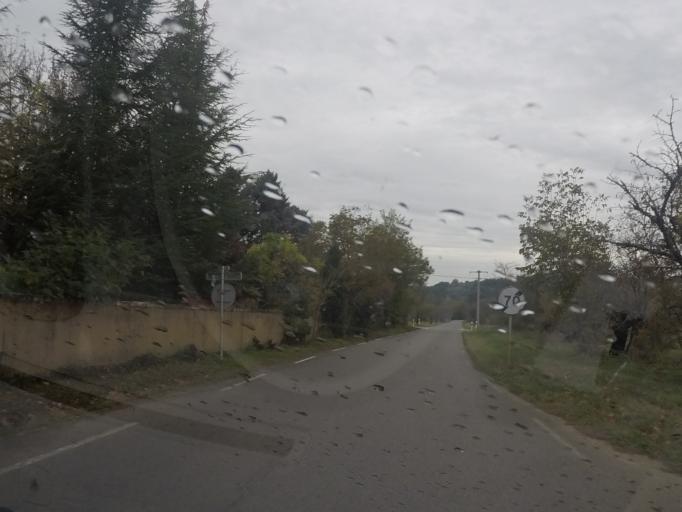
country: FR
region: Provence-Alpes-Cote d'Azur
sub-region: Departement du Vaucluse
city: Goult
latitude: 43.8547
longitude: 5.2731
